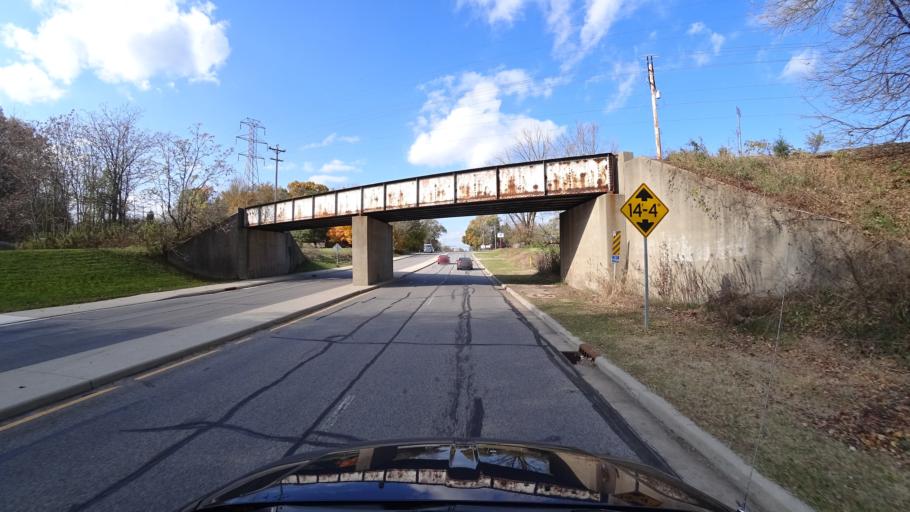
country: US
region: Indiana
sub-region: LaPorte County
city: Trail Creek
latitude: 41.7064
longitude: -86.8600
